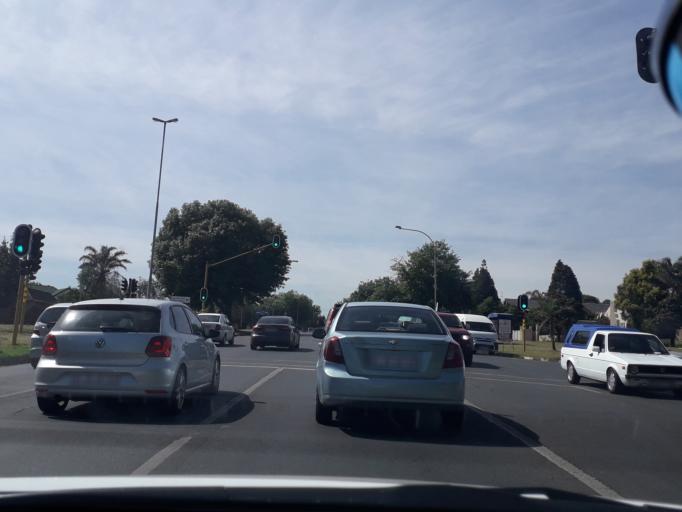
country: ZA
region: Gauteng
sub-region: City of Johannesburg Metropolitan Municipality
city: Johannesburg
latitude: -26.1563
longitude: 27.9920
